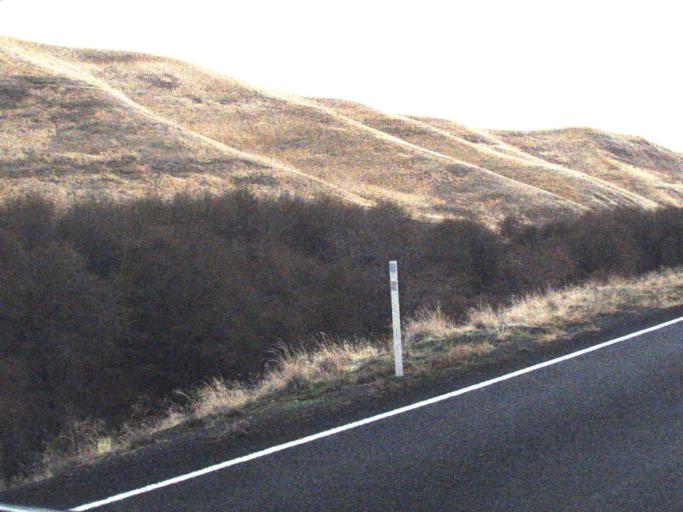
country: US
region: Washington
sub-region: Columbia County
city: Dayton
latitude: 46.5066
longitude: -118.0106
